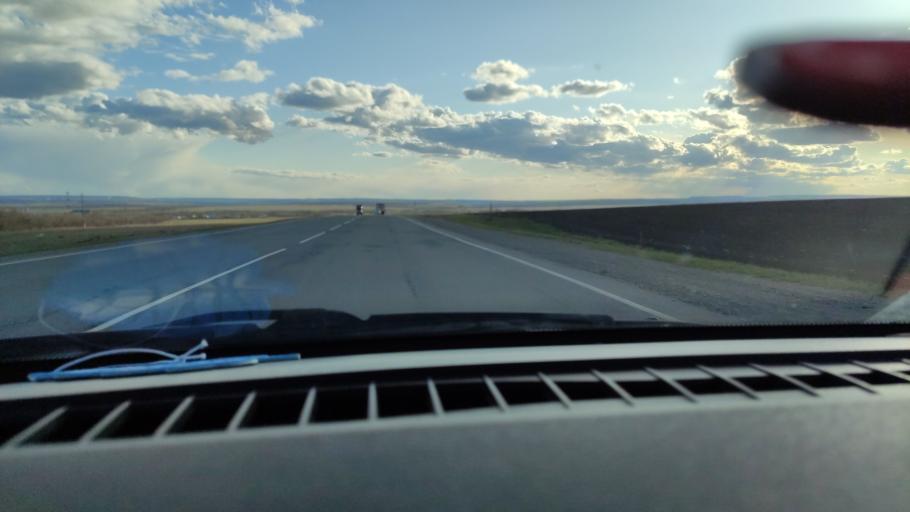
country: RU
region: Saratov
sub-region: Saratovskiy Rayon
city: Saratov
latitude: 51.7423
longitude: 46.0470
